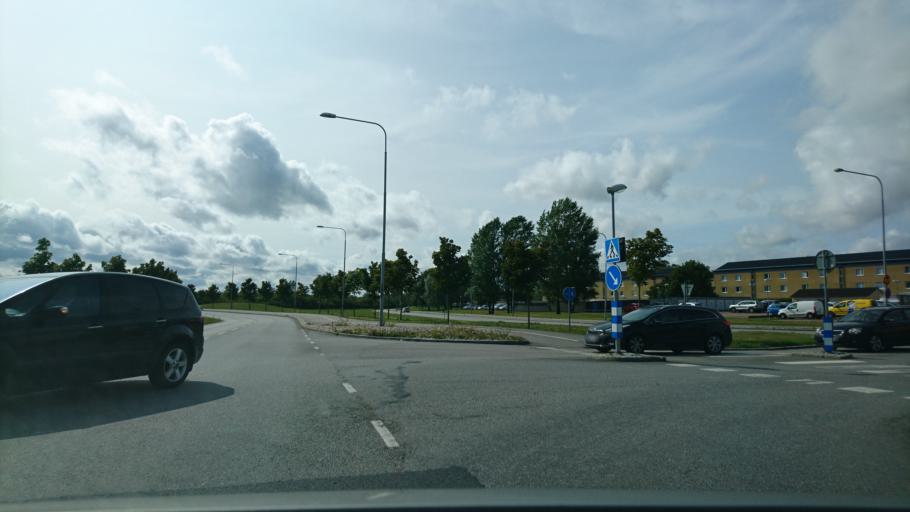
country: SE
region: Uppsala
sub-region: Uppsala Kommun
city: Gamla Uppsala
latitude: 59.8856
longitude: 17.6574
